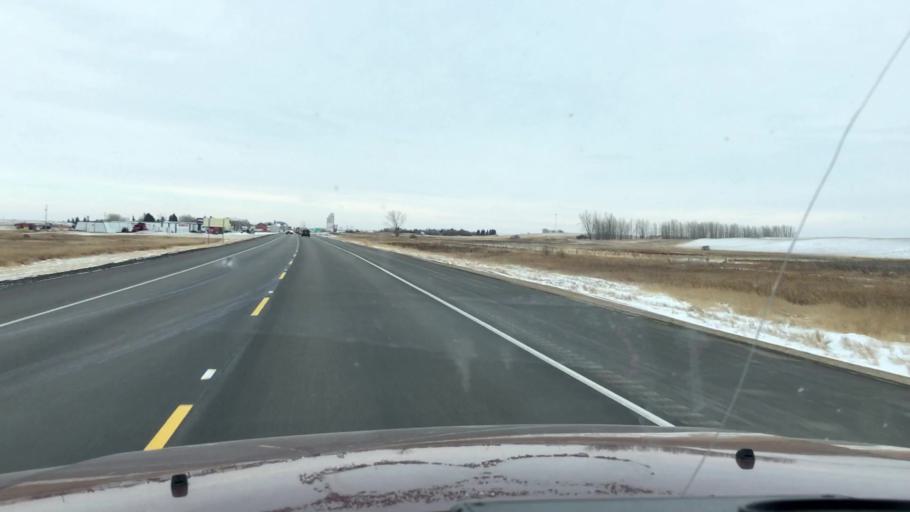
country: CA
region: Saskatchewan
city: Moose Jaw
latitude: 50.8577
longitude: -105.5814
